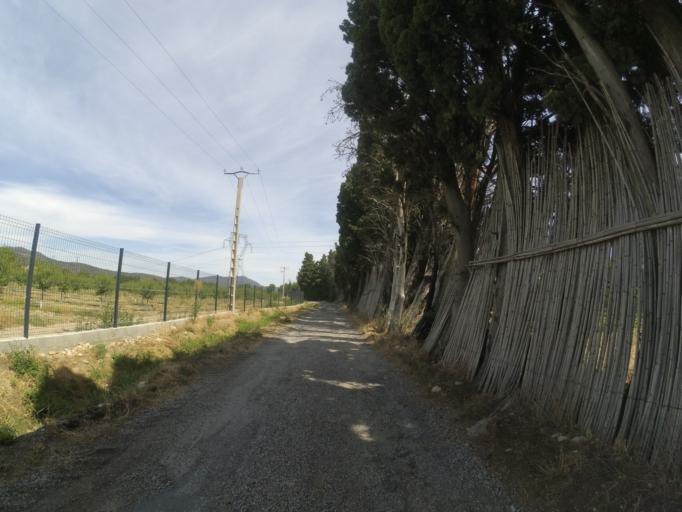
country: FR
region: Languedoc-Roussillon
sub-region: Departement des Pyrenees-Orientales
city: Ille-sur-Tet
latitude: 42.6782
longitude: 2.6382
